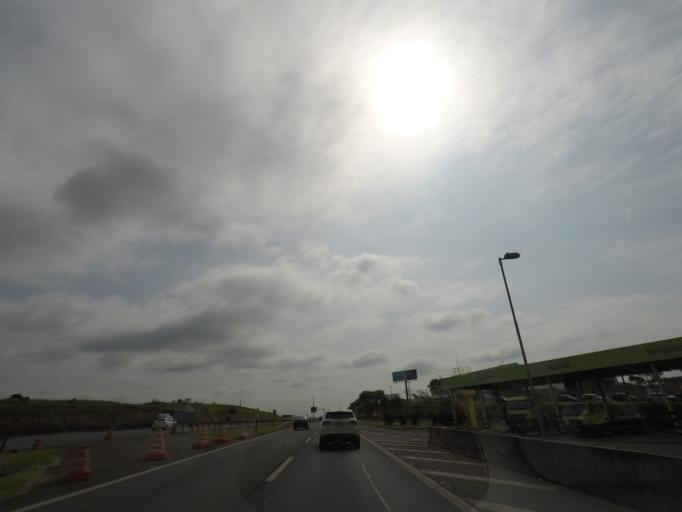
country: BR
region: Sao Paulo
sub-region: Campinas
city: Campinas
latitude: -22.8453
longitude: -47.0773
